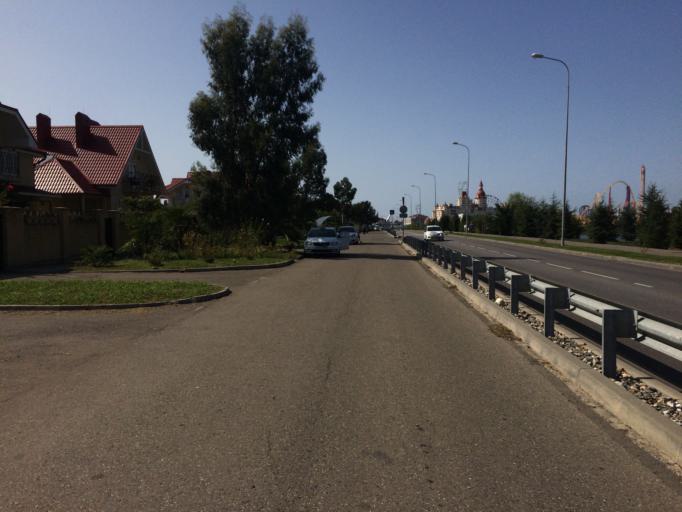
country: RU
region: Krasnodarskiy
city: Adler
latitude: 43.3990
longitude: 39.9733
